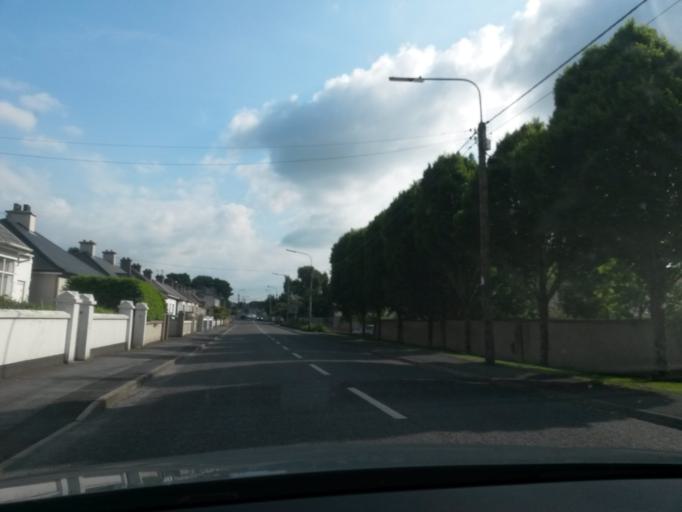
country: IE
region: Munster
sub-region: An Clar
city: Ennis
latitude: 52.8421
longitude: -8.9766
